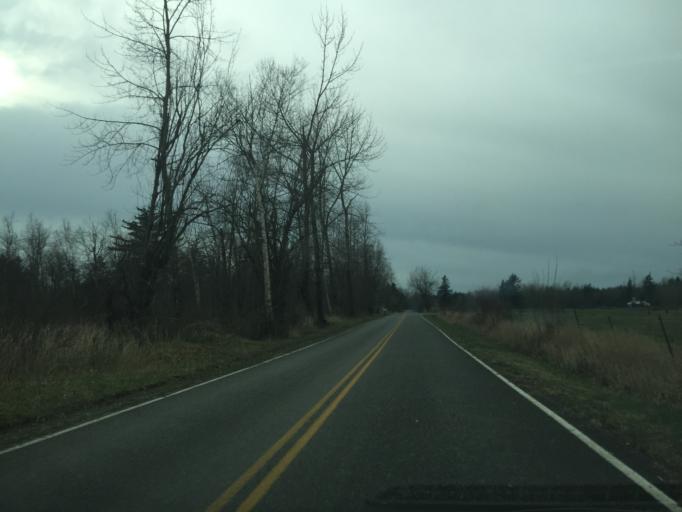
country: US
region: Washington
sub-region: Whatcom County
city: Everson
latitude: 48.9493
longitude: -122.3675
